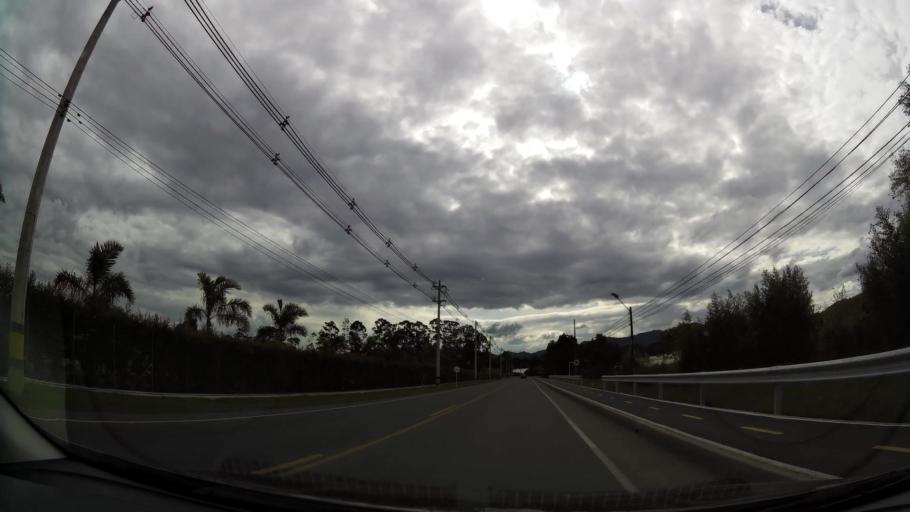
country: CO
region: Antioquia
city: Rionegro
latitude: 6.1459
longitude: -75.4273
